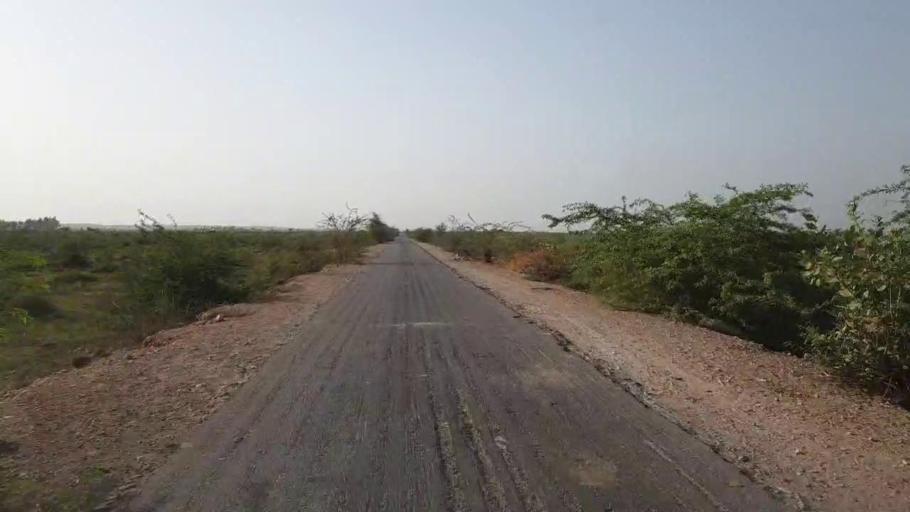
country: PK
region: Sindh
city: Jam Sahib
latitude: 26.4411
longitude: 68.8663
